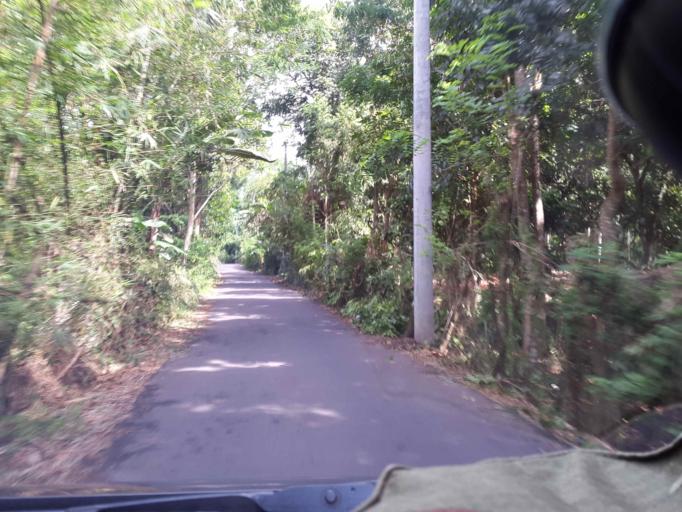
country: ID
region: West Nusa Tenggara
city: Sesaot Lauq
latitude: -8.5612
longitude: 116.2338
